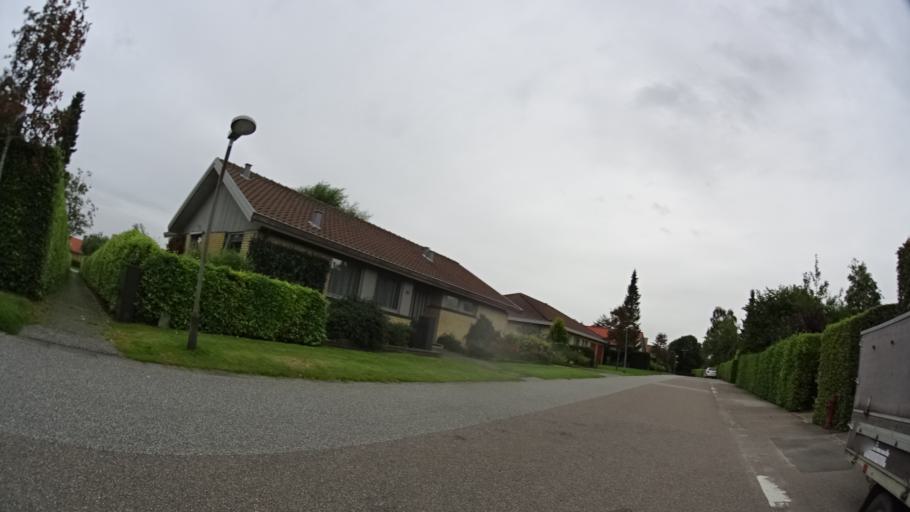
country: DK
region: Central Jutland
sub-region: Arhus Kommune
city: Stavtrup
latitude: 56.1652
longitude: 10.1589
